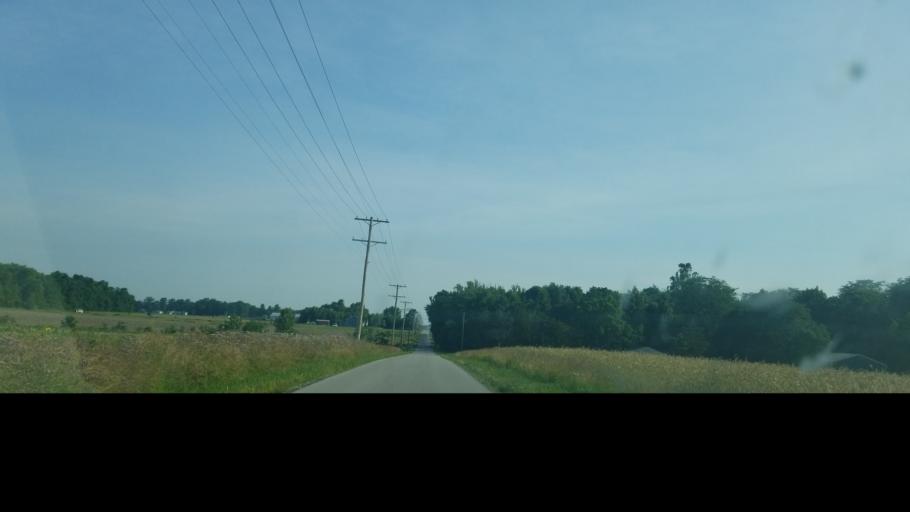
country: US
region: Ohio
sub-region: Hancock County
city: Arlington
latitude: 40.8607
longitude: -83.6701
